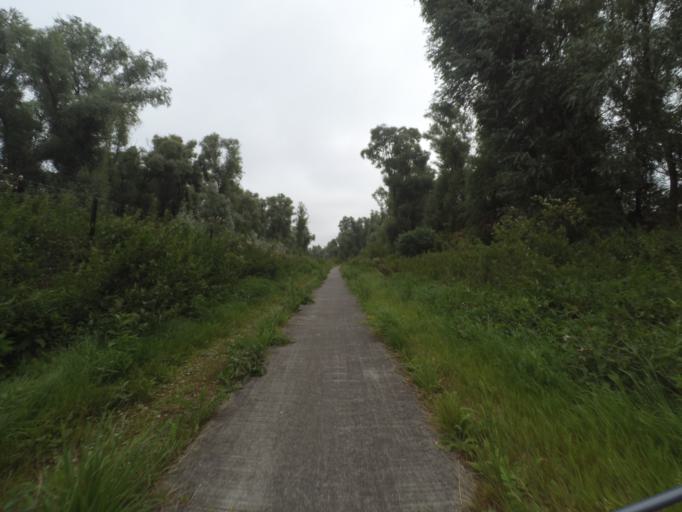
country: NL
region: Flevoland
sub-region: Gemeente Lelystad
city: Lelystad
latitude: 52.4373
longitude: 5.4189
